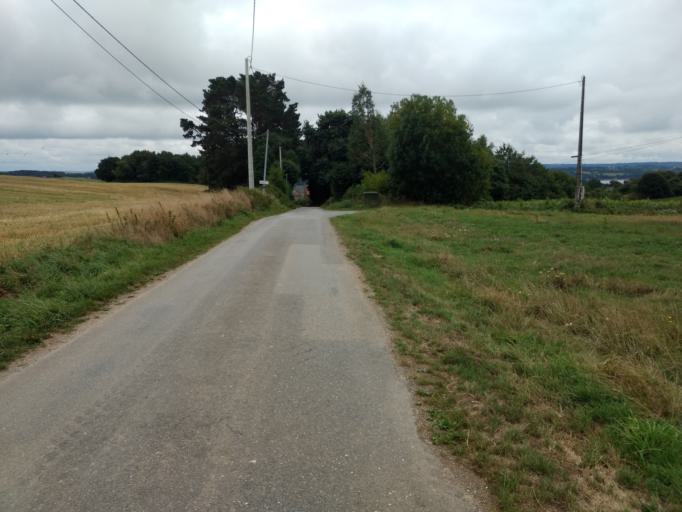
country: FR
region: Brittany
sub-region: Departement du Finistere
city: Loperhet
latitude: 48.3638
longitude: -4.2893
